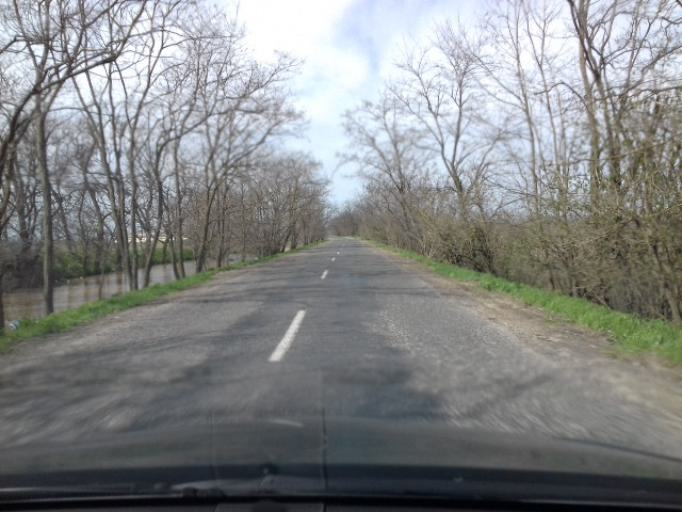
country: HU
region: Jasz-Nagykun-Szolnok
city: Cserkeszolo
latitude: 46.8860
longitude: 20.1497
